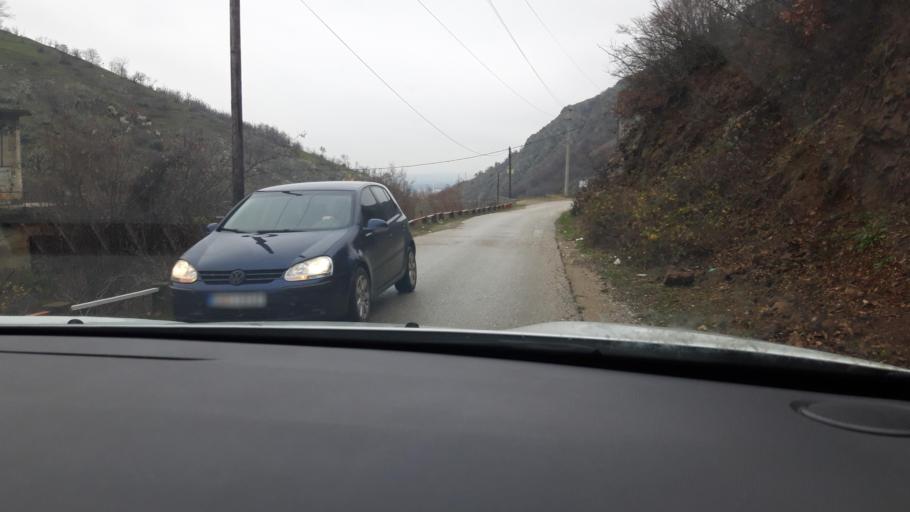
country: MK
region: Opstina Lipkovo
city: Lipkovo
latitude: 42.1658
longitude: 21.5728
